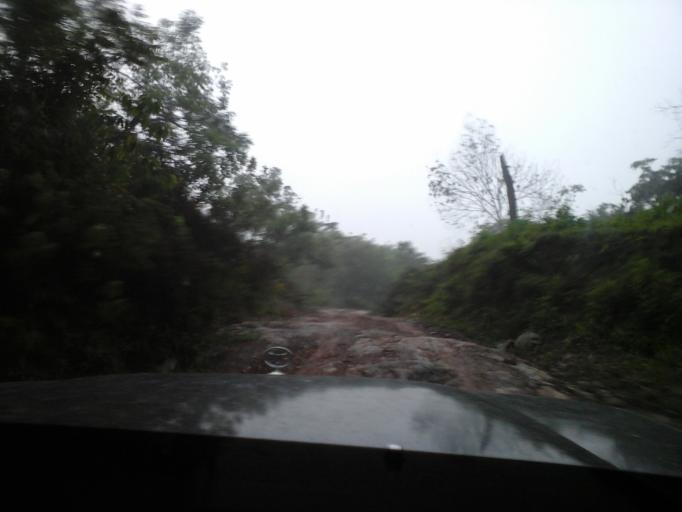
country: CO
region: Cesar
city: Agustin Codazzi
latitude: 9.9388
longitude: -73.1460
